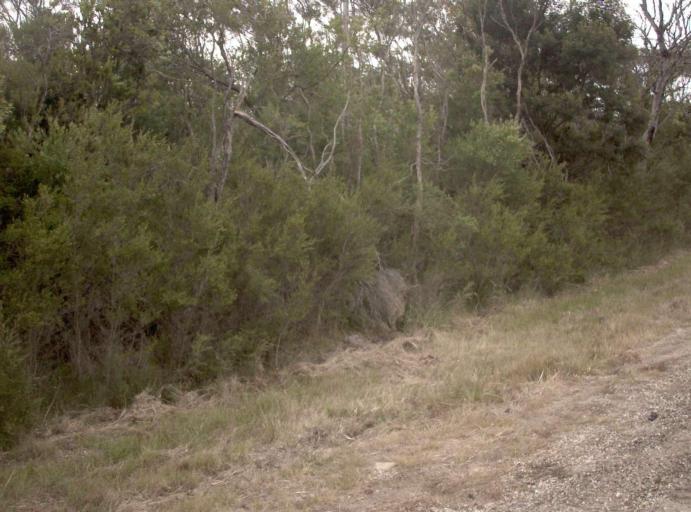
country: AU
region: Victoria
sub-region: East Gippsland
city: Bairnsdale
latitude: -38.1293
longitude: 147.4264
